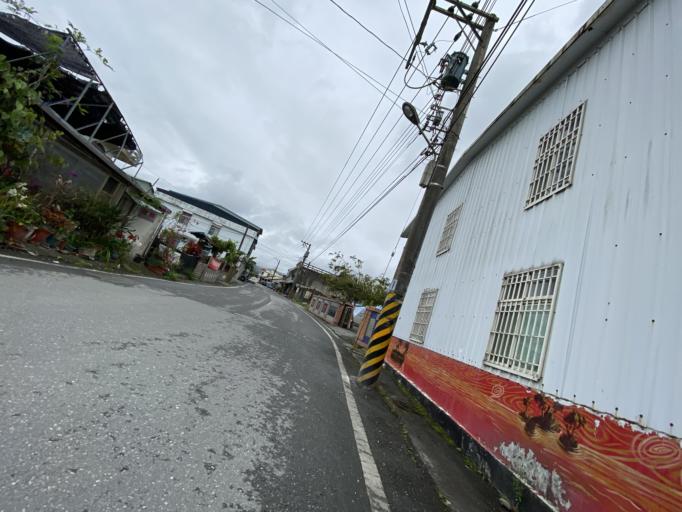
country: TW
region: Taiwan
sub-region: Hualien
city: Hualian
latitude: 23.6582
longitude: 121.4505
